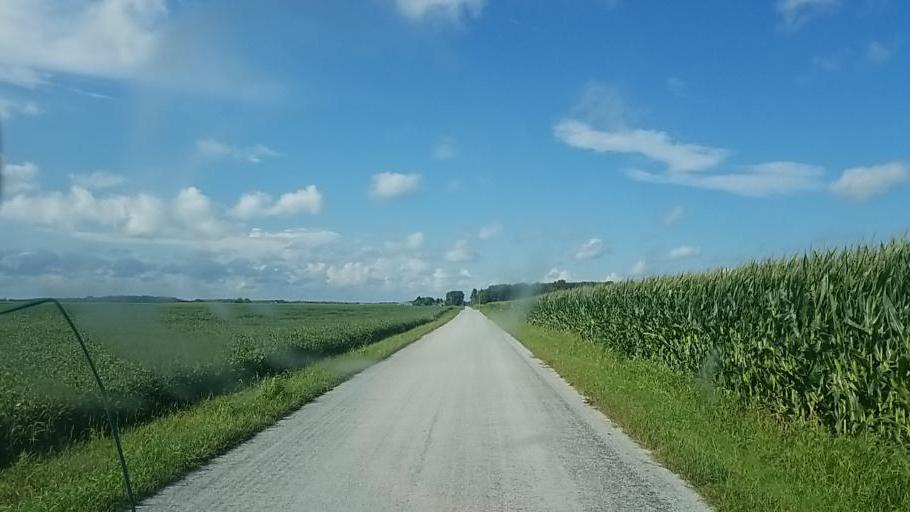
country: US
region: Ohio
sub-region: Hardin County
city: Kenton
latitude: 40.6843
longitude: -83.5309
